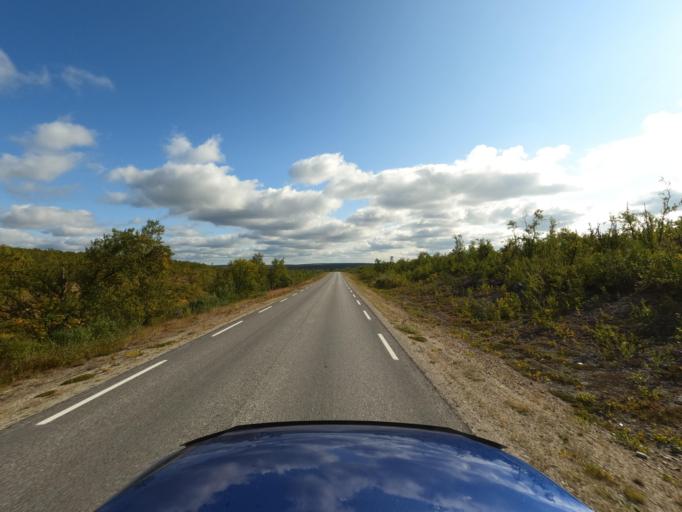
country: NO
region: Finnmark Fylke
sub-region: Porsanger
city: Lakselv
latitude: 69.3939
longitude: 24.5711
